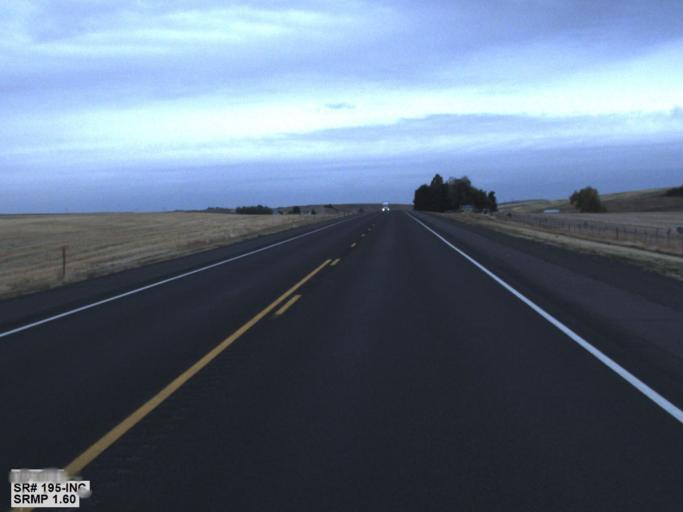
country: US
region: Washington
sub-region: Asotin County
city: Clarkston
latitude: 46.4885
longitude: -117.0716
